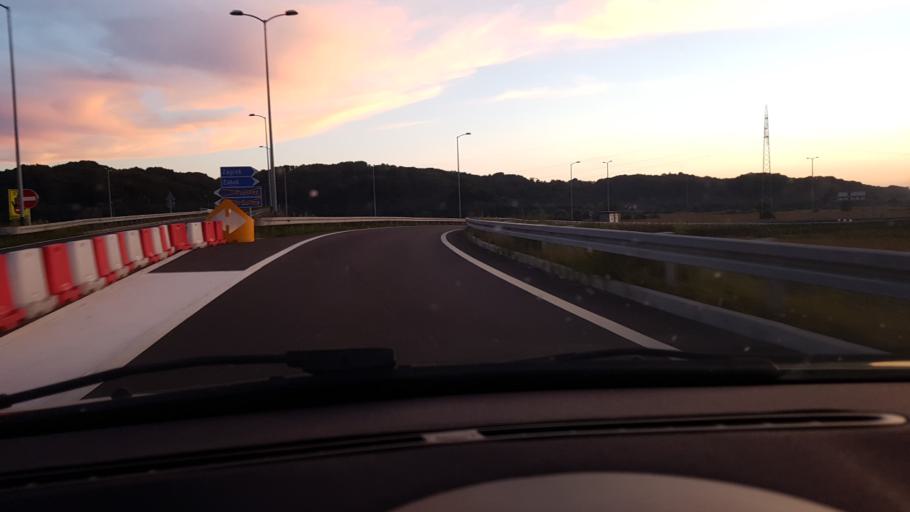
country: HR
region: Krapinsko-Zagorska
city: Selnica
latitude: 46.0386
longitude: 16.0760
